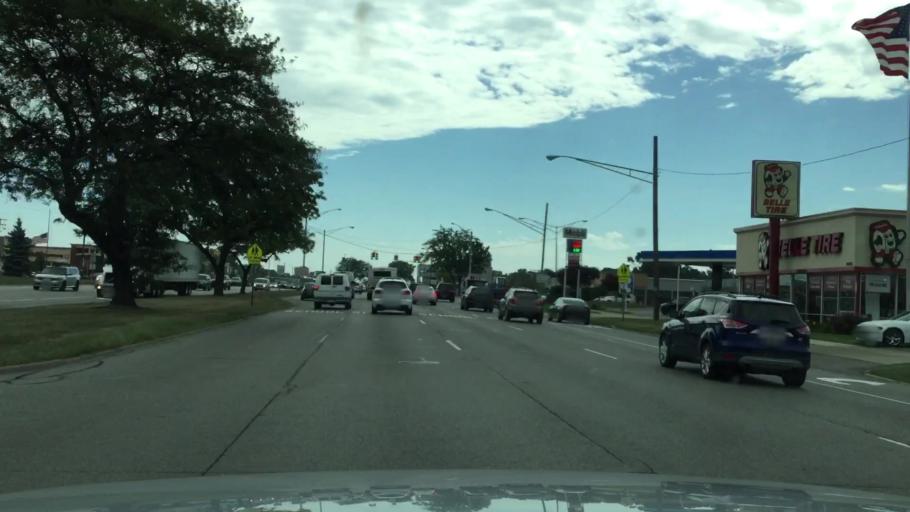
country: US
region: Michigan
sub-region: Oakland County
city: Berkley
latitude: 42.5190
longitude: -83.1874
